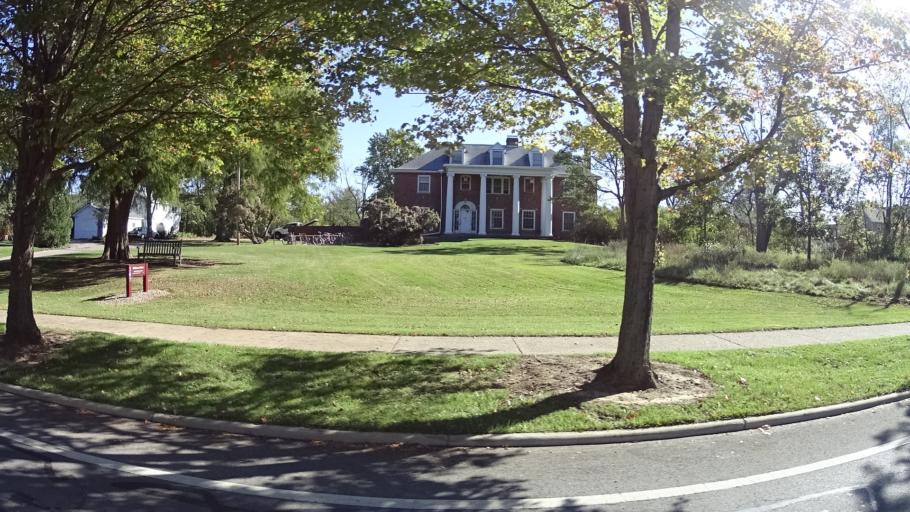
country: US
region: Ohio
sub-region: Lorain County
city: Oberlin
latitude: 41.2862
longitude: -82.2202
